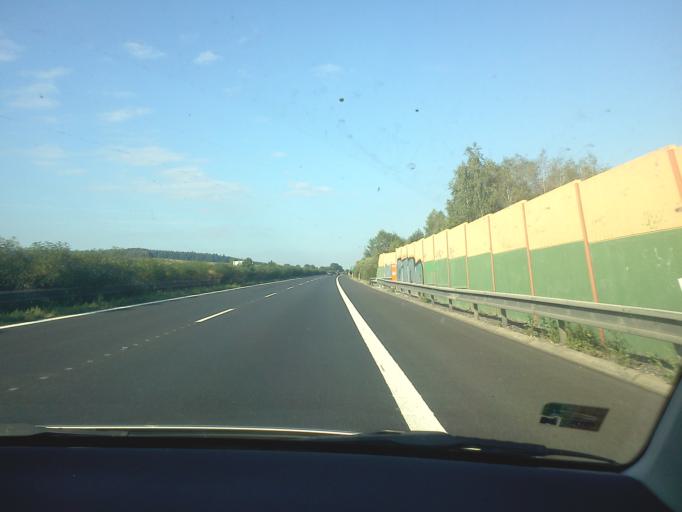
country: CZ
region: Central Bohemia
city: Komarov
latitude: 49.8450
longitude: 13.8412
